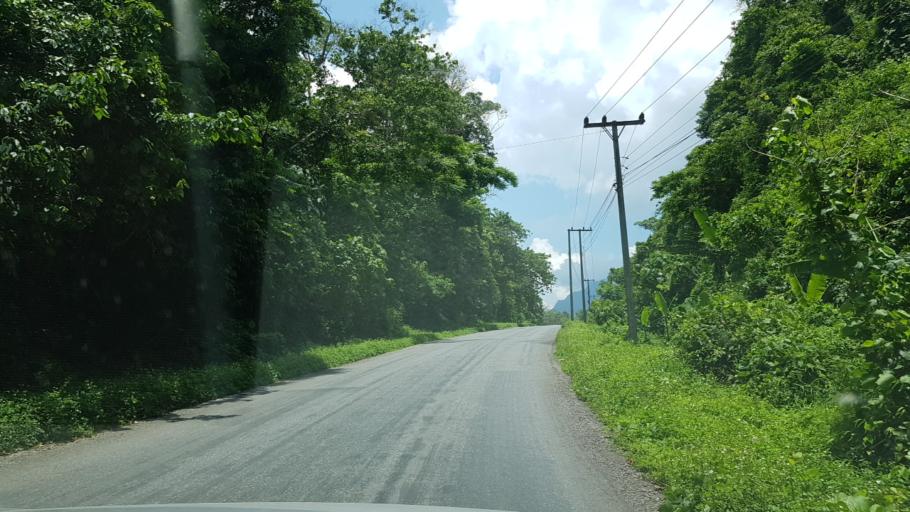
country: LA
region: Vientiane
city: Muang Kasi
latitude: 19.1387
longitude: 102.2949
